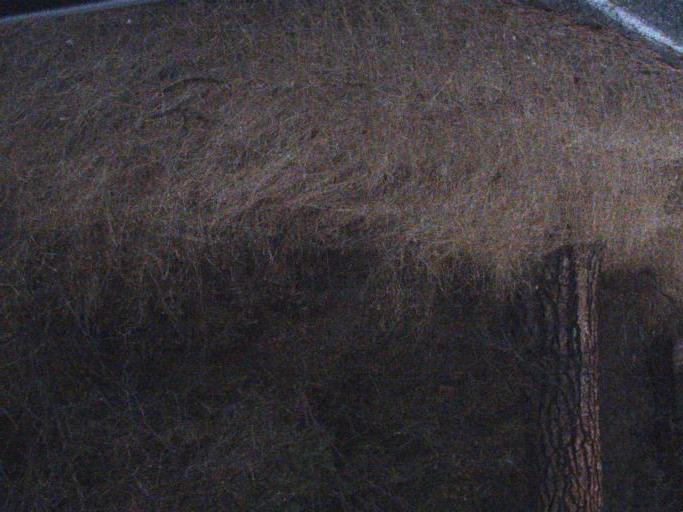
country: US
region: Washington
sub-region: Ferry County
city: Republic
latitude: 48.5717
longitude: -118.7468
